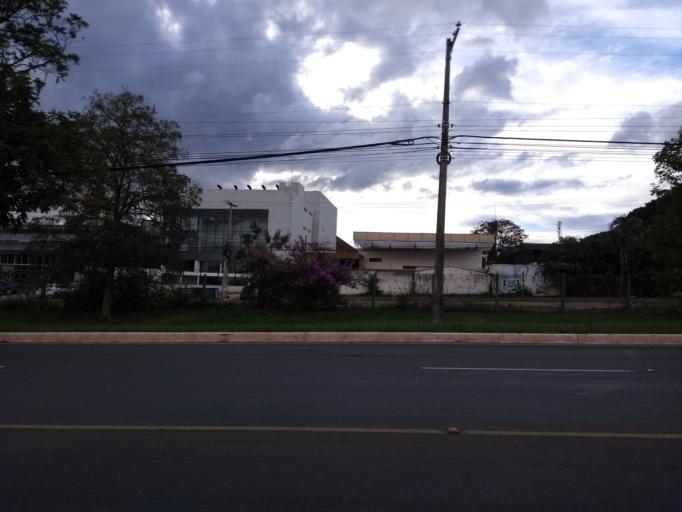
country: BR
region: Federal District
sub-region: Brasilia
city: Brasilia
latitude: -15.7918
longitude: -47.9093
